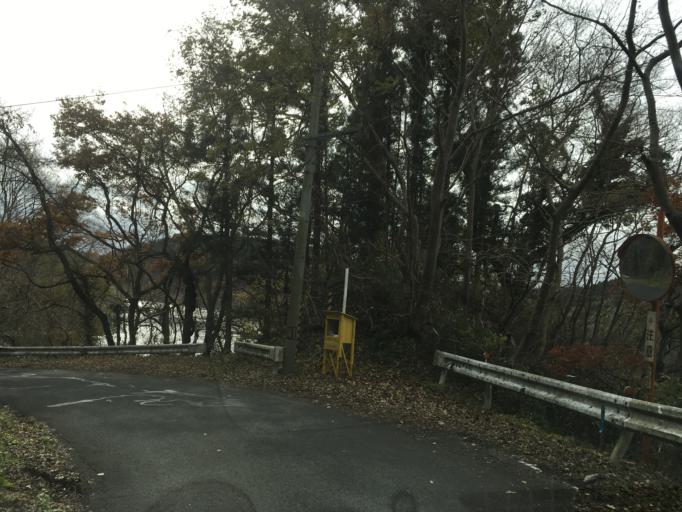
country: JP
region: Iwate
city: Ichinoseki
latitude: 38.7858
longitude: 141.2643
